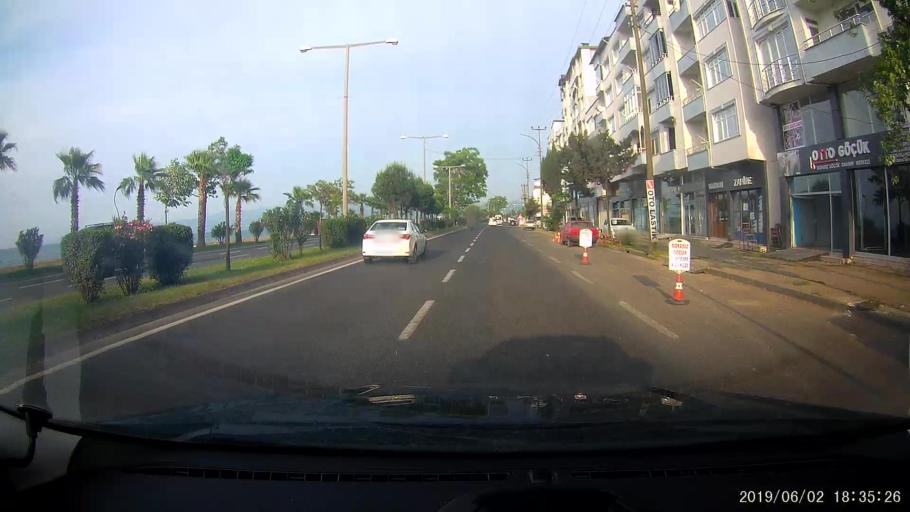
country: TR
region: Ordu
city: Fatsa
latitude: 41.0264
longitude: 37.5161
